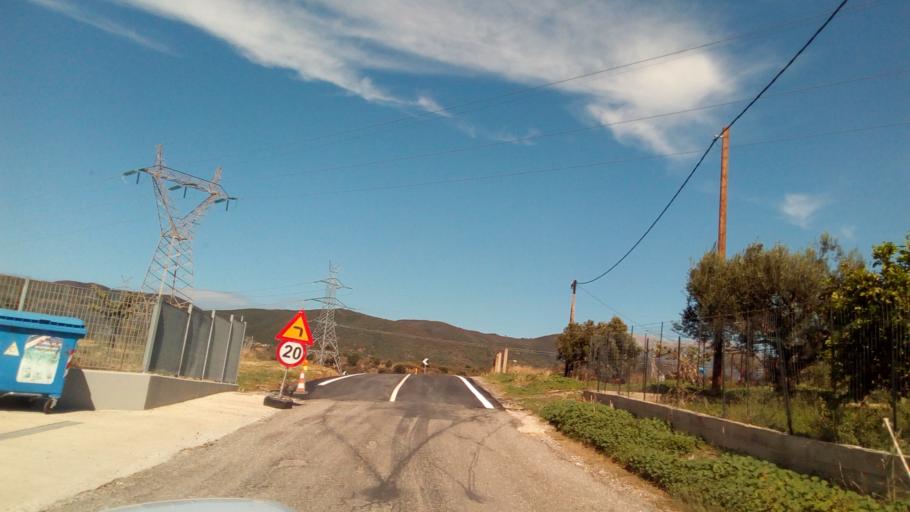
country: GR
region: West Greece
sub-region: Nomos Aitolias kai Akarnanias
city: Antirrio
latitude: 38.3440
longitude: 21.7554
